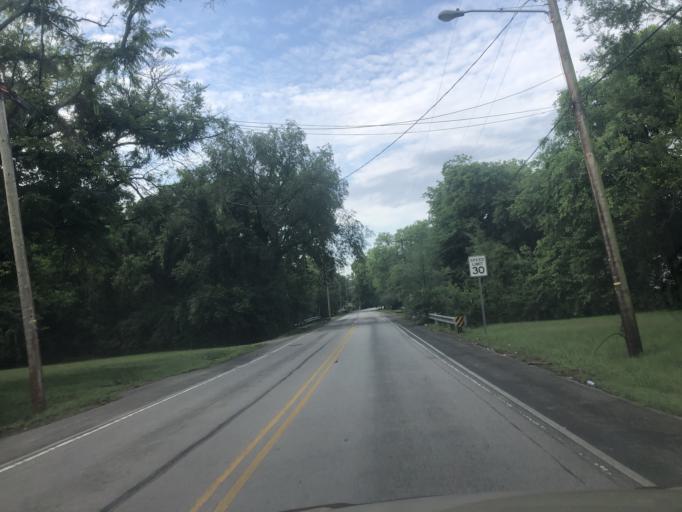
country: US
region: Tennessee
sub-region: Davidson County
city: Goodlettsville
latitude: 36.2553
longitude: -86.7073
